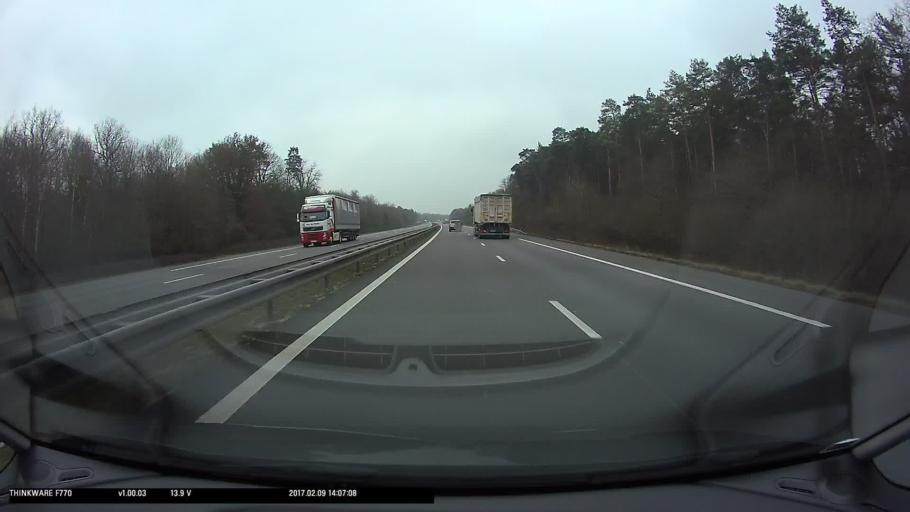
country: FR
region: Centre
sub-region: Departement du Loir-et-Cher
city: Nouan-le-Fuzelier
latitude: 47.4917
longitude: 2.0070
